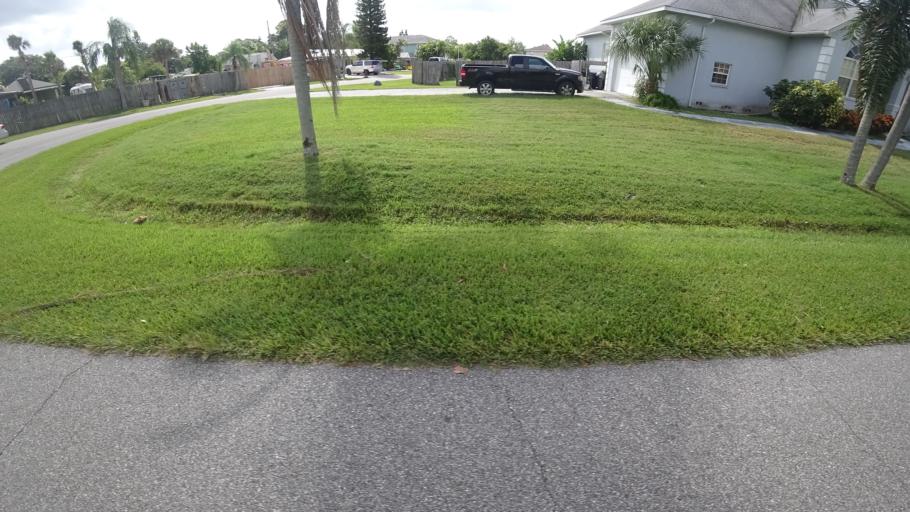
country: US
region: Florida
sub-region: Manatee County
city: Memphis
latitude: 27.5583
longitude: -82.5699
